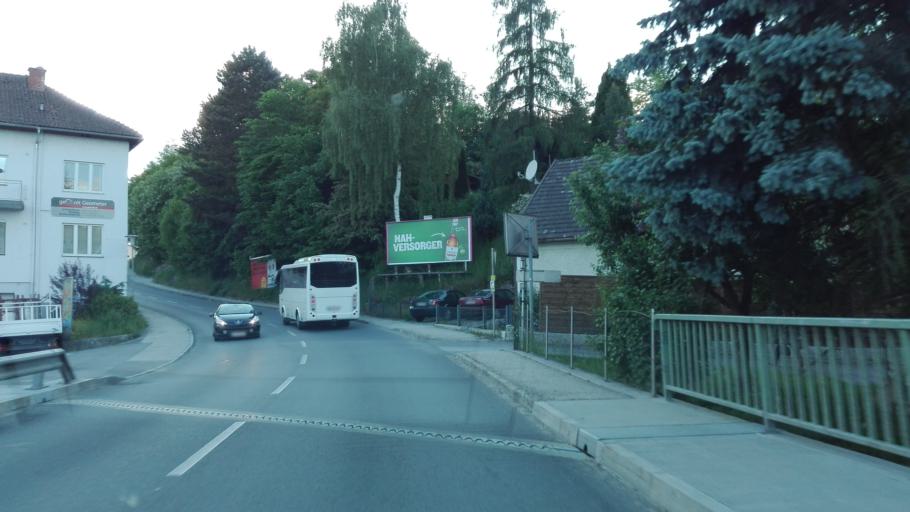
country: AT
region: Upper Austria
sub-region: Politischer Bezirk Urfahr-Umgebung
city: Engerwitzdorf
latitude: 48.3552
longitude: 14.5251
